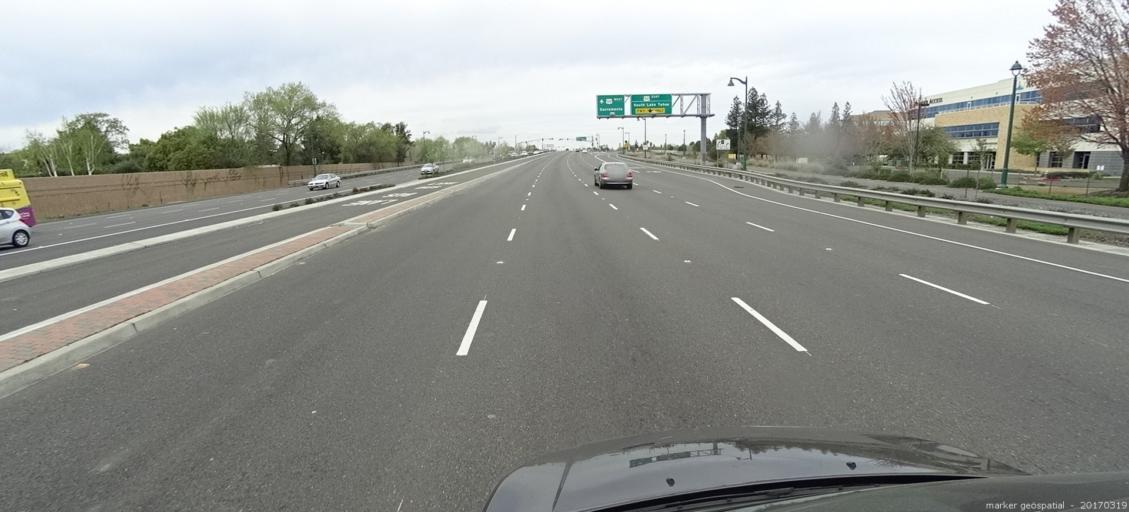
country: US
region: California
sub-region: Sacramento County
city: Rosemont
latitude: 38.5552
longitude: -121.3768
